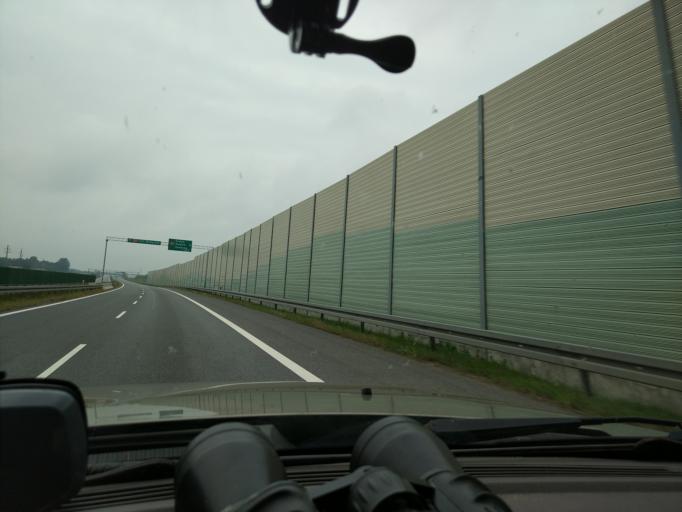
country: PL
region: Podlasie
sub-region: Powiat zambrowski
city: Zambrow
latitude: 52.9677
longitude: 22.2052
